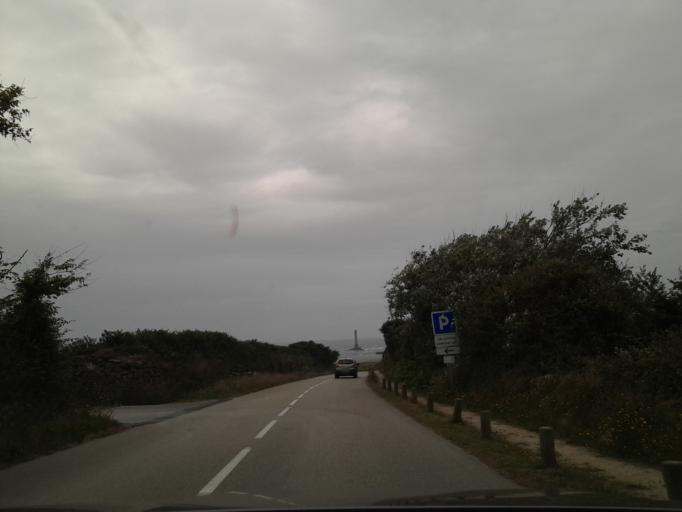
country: FR
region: Lower Normandy
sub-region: Departement de la Manche
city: Beaumont-Hague
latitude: 49.7146
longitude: -1.9344
